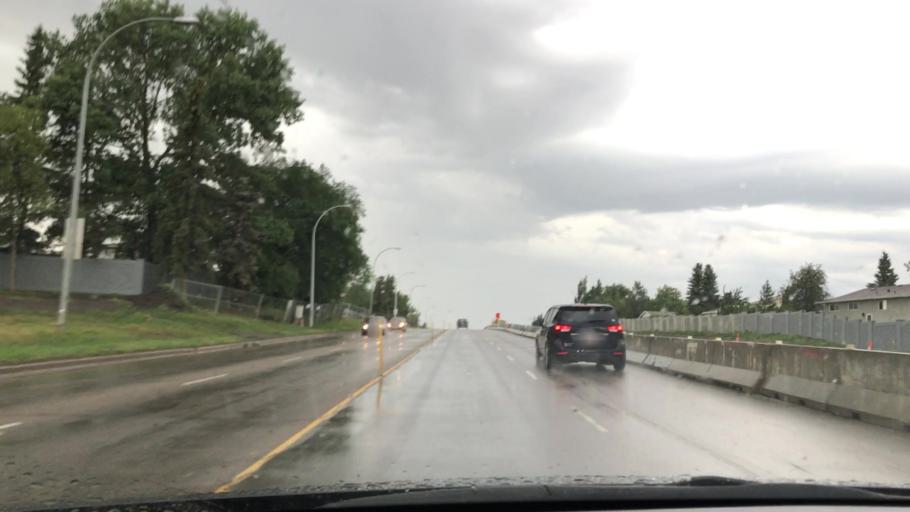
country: CA
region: Alberta
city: Edmonton
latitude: 53.4670
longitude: -113.4368
